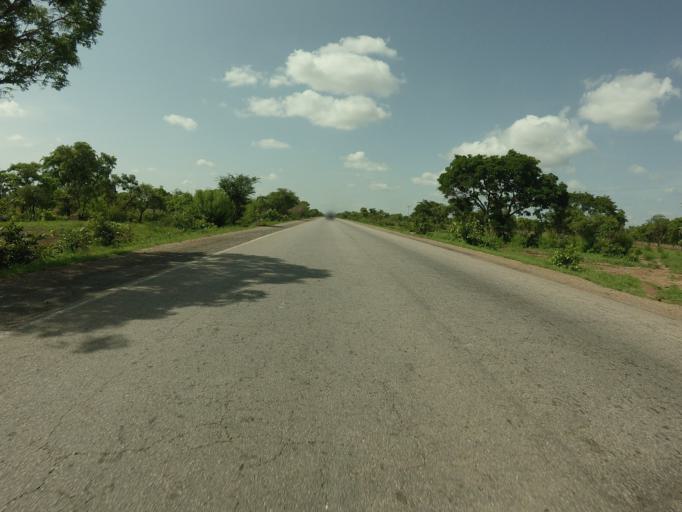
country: GH
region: Northern
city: Savelugu
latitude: 9.9479
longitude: -0.8378
